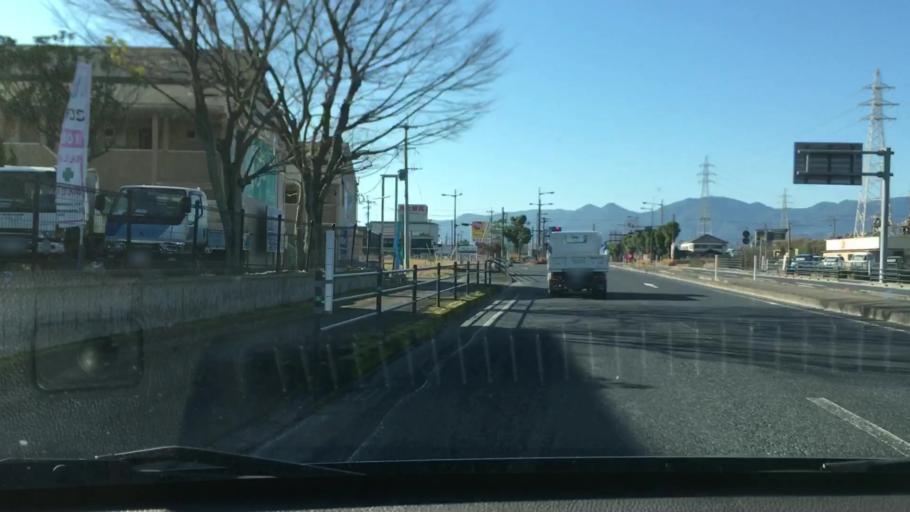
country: JP
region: Kagoshima
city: Kajiki
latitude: 31.7382
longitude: 130.6507
